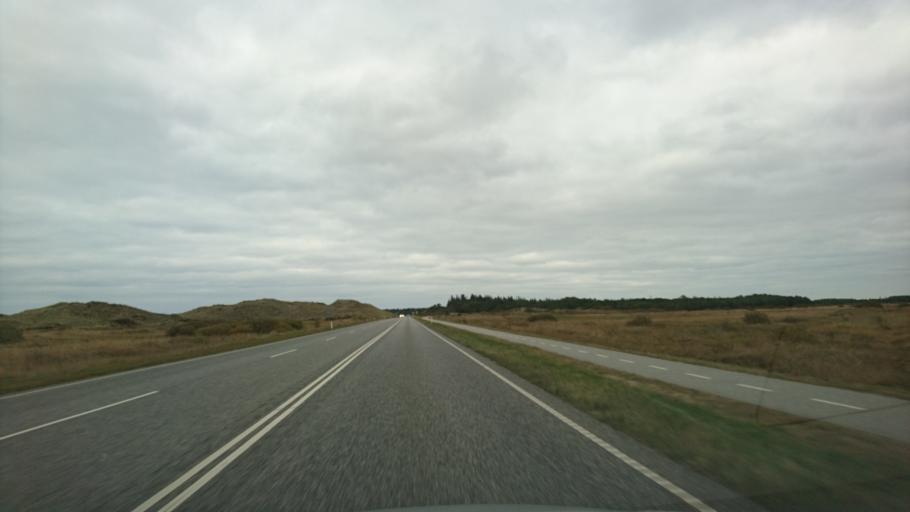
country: DK
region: North Denmark
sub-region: Frederikshavn Kommune
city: Skagen
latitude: 57.6924
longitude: 10.4734
